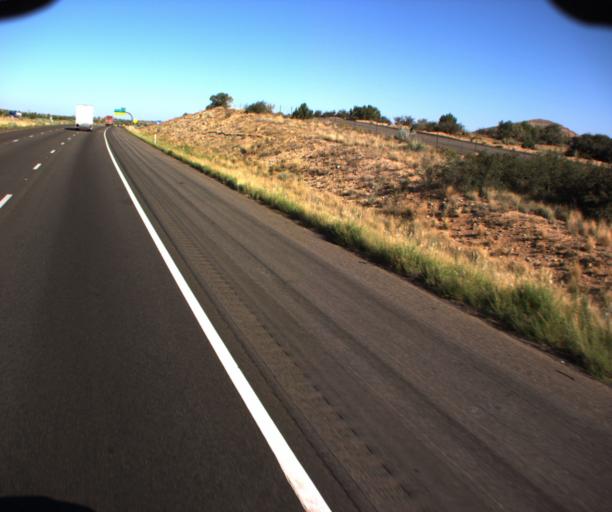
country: US
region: Arizona
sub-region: Mohave County
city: New Kingman-Butler
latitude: 35.1713
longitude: -113.7741
